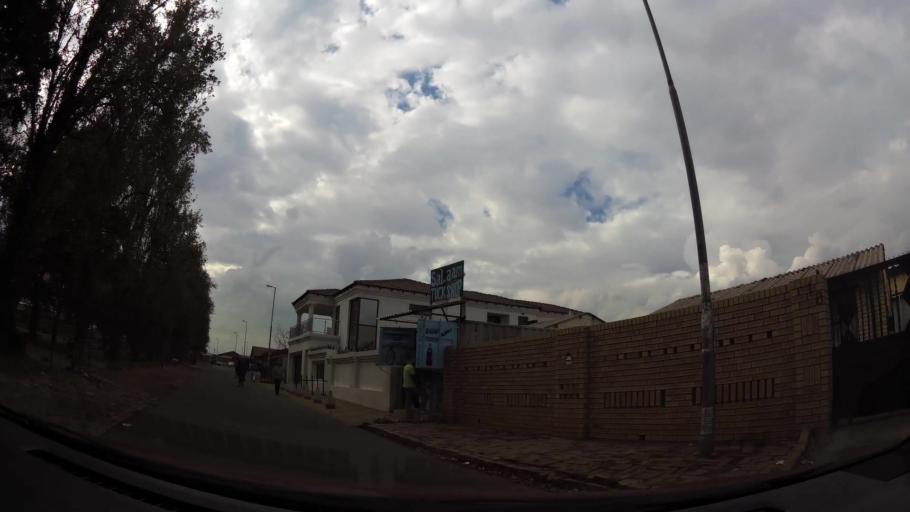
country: ZA
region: Gauteng
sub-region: City of Johannesburg Metropolitan Municipality
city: Soweto
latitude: -26.2513
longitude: 27.8490
